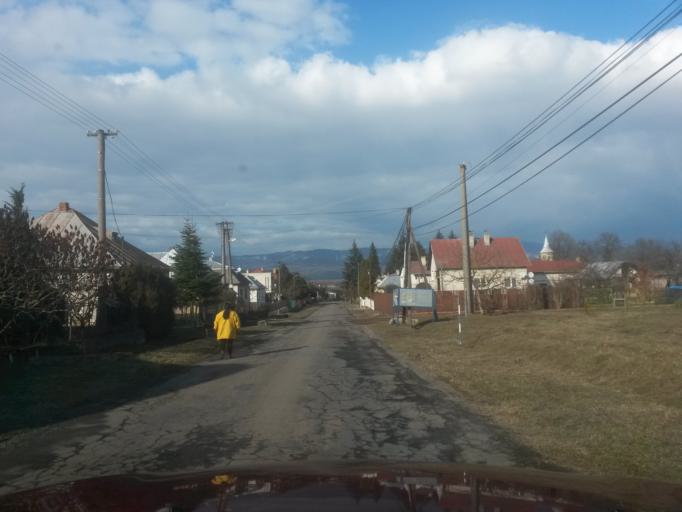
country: SK
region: Kosicky
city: Sobrance
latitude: 48.7686
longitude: 22.0852
